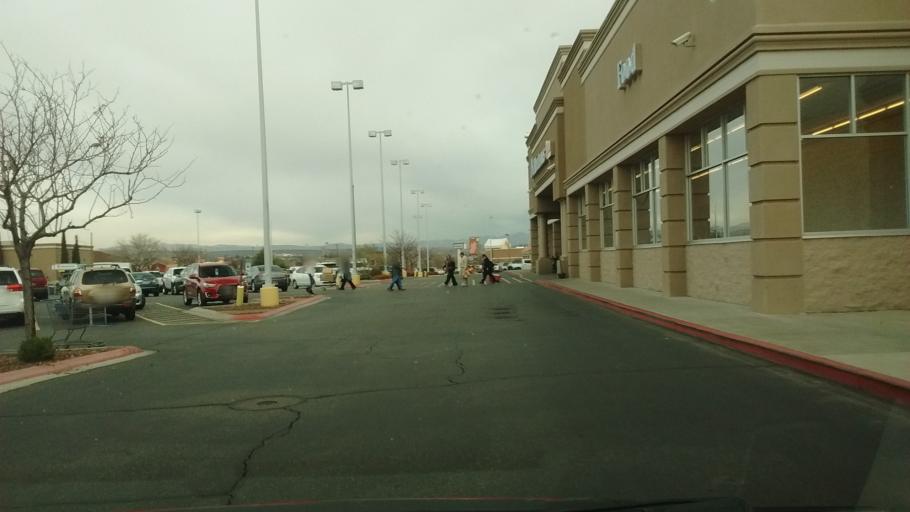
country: US
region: Utah
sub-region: Washington County
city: Washington
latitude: 37.1256
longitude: -113.5252
